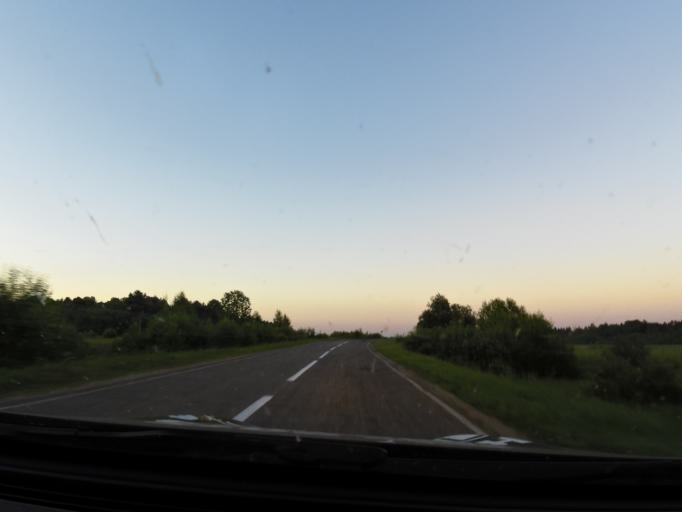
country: RU
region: Jaroslavl
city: Lyubim
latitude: 58.3369
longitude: 41.0799
